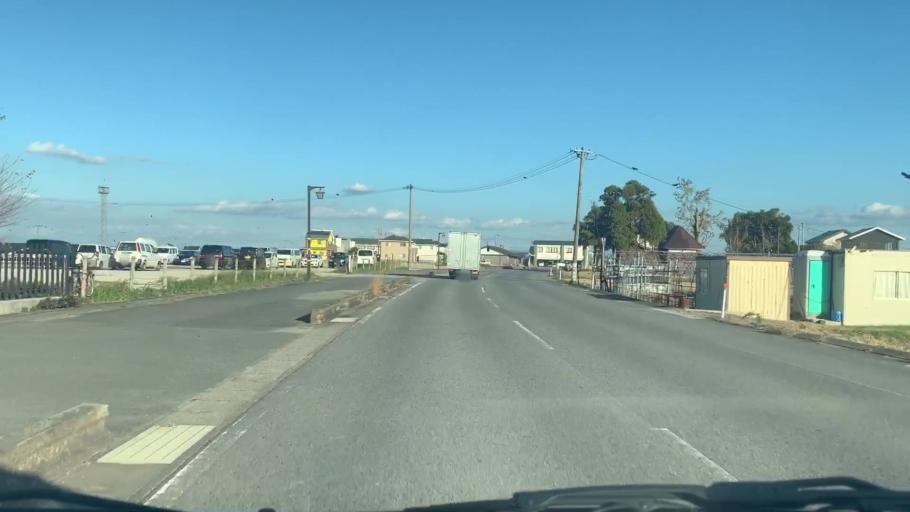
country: JP
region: Saga Prefecture
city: Kanzakimachi-kanzaki
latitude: 33.2680
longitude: 130.3673
